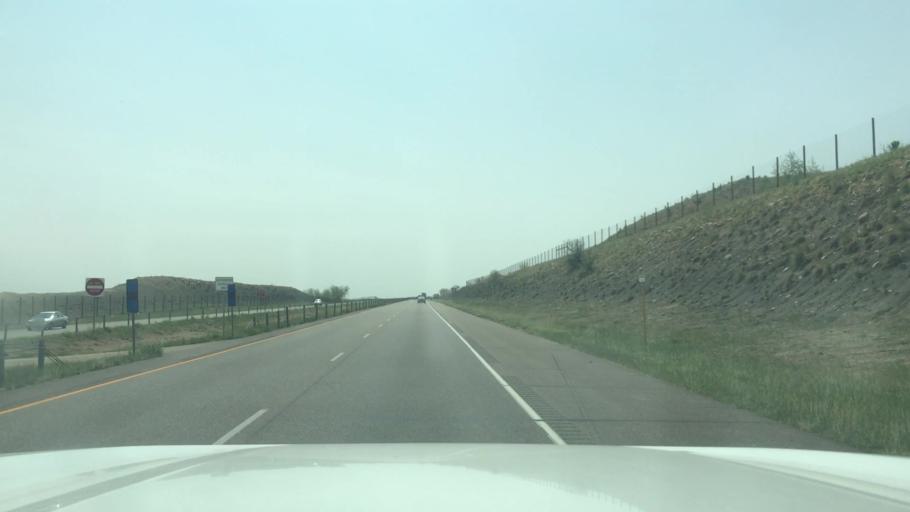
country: US
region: Colorado
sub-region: El Paso County
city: Fountain
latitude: 38.6497
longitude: -104.6964
